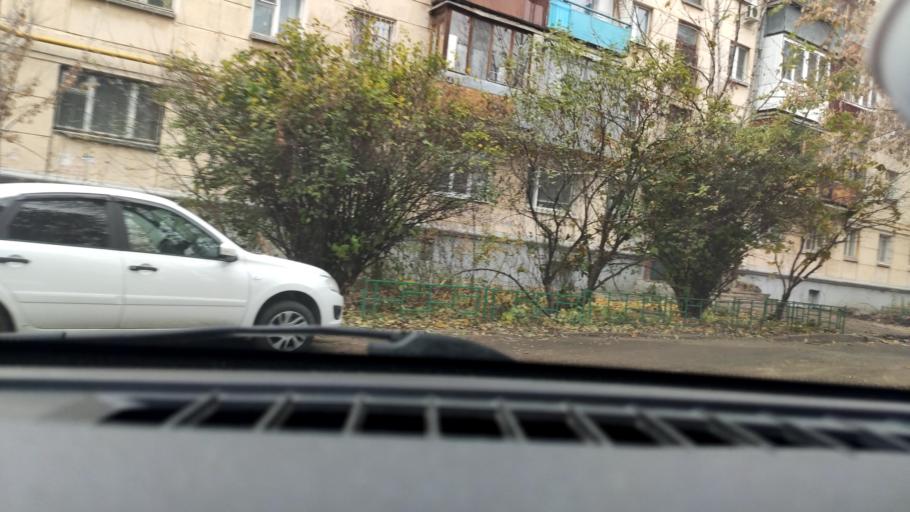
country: RU
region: Samara
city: Samara
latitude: 53.2254
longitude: 50.2625
